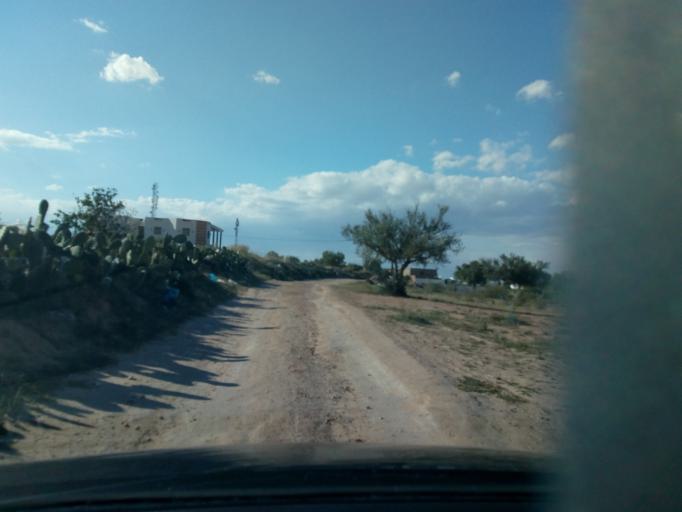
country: TN
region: Safaqis
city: Sfax
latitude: 34.7249
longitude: 10.6101
